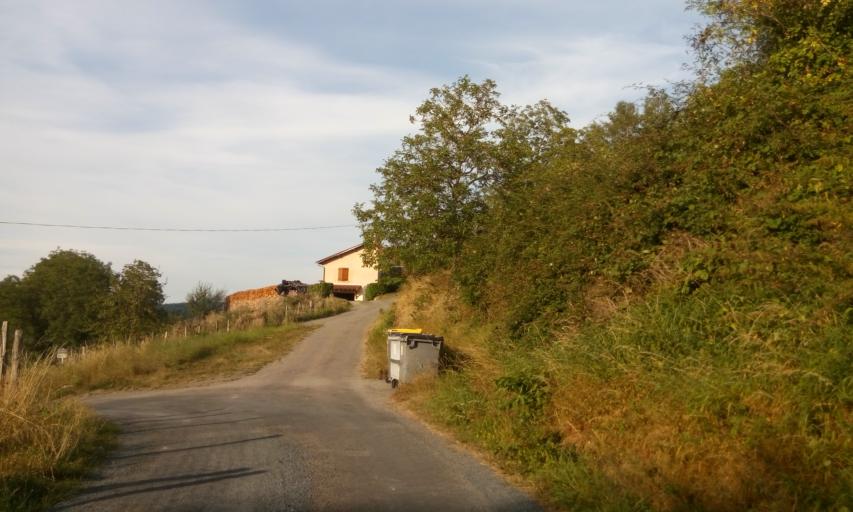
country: FR
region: Rhone-Alpes
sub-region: Departement du Rhone
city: Grandris
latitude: 45.9978
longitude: 4.4569
